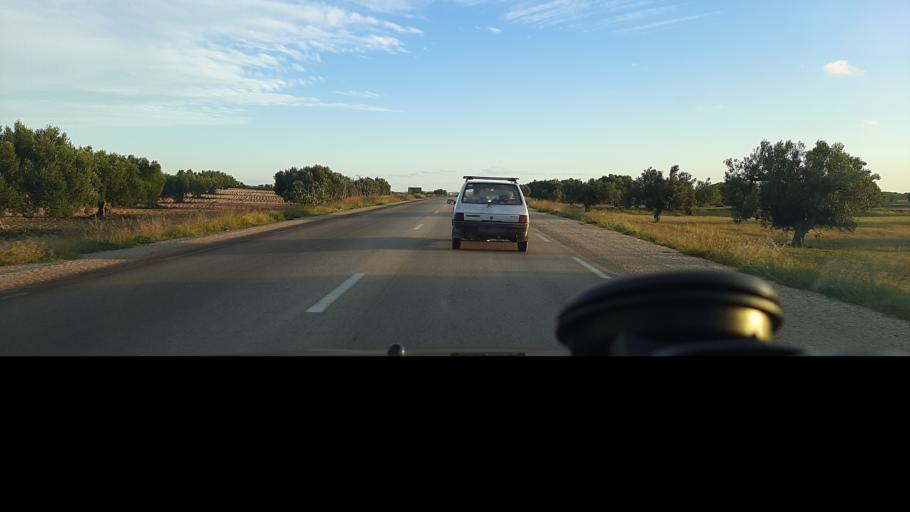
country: TN
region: Safaqis
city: Sfax
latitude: 34.9237
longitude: 10.6262
